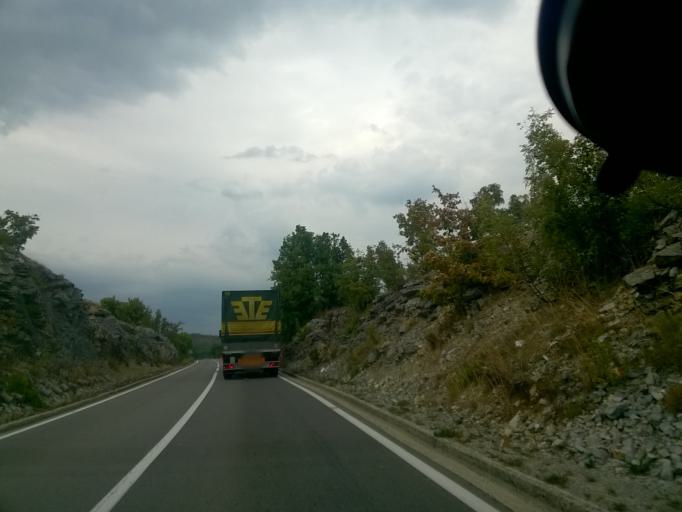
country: ME
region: Kotor
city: Risan
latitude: 42.7460
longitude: 18.6435
